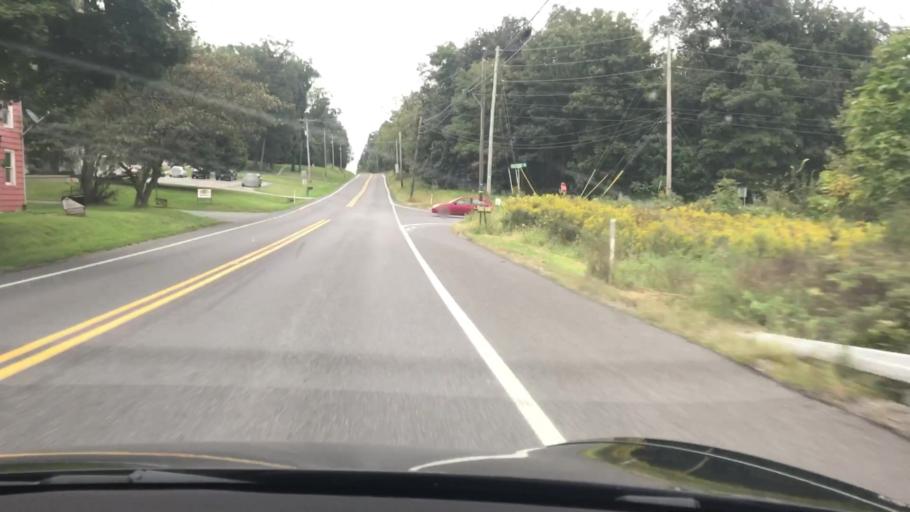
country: US
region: Pennsylvania
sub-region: Adams County
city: Lake Meade
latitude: 39.9492
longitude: -77.1324
